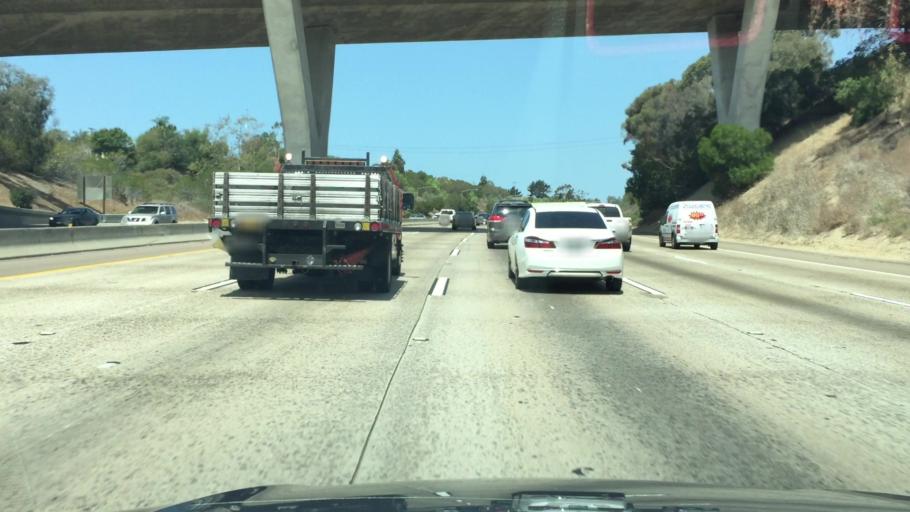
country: US
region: California
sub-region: San Diego County
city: San Diego
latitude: 32.7852
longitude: -117.1449
